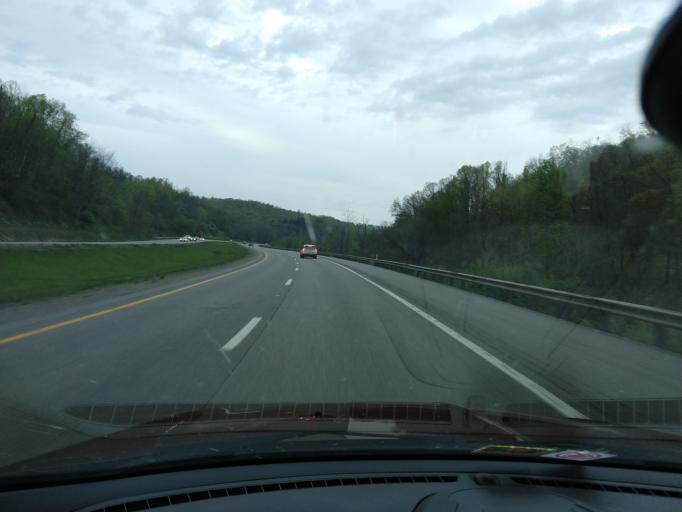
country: US
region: West Virginia
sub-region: Lewis County
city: Weston
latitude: 39.0654
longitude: -80.4025
